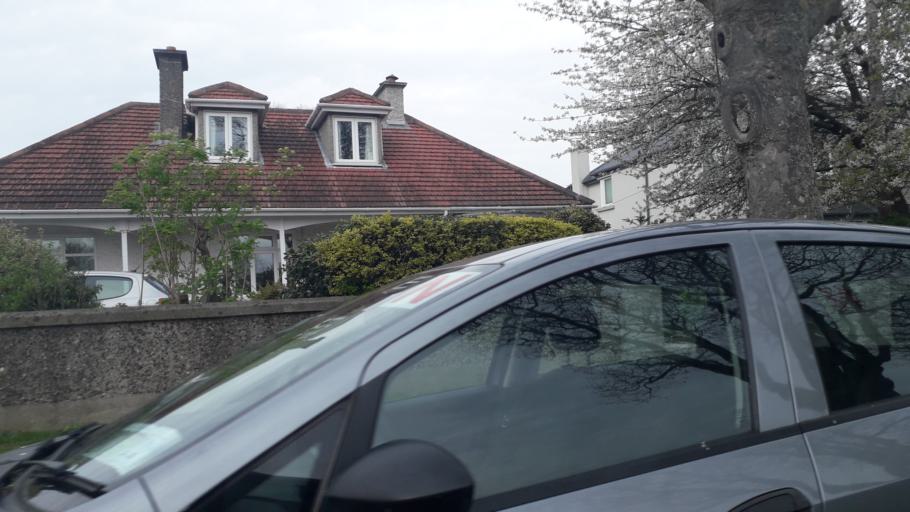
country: IE
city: Killester
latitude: 53.3626
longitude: -6.1978
